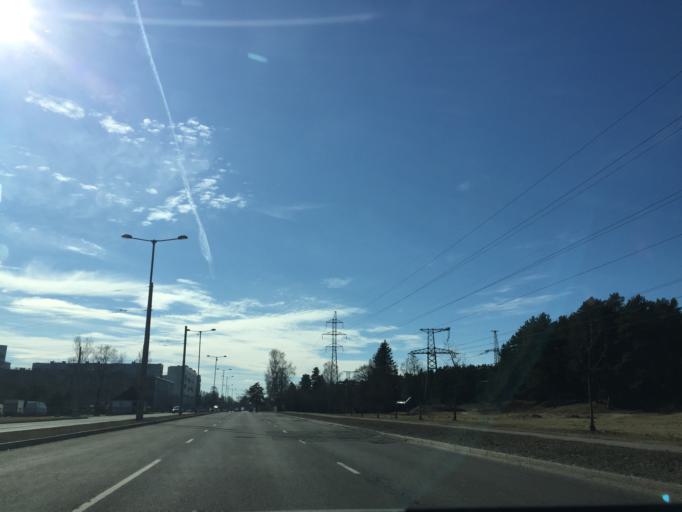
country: LV
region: Marupe
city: Marupe
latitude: 56.9674
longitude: 24.0082
